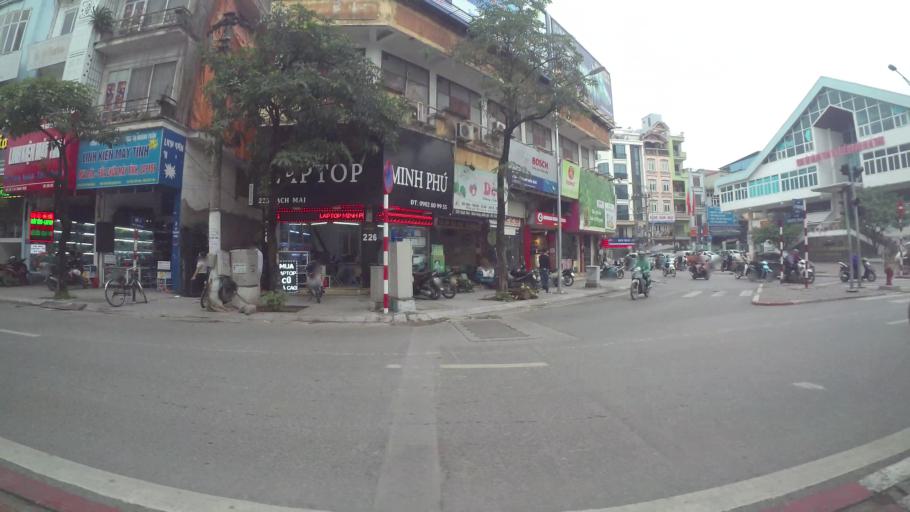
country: VN
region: Ha Noi
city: Hai BaTrung
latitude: 21.0032
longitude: 105.8508
